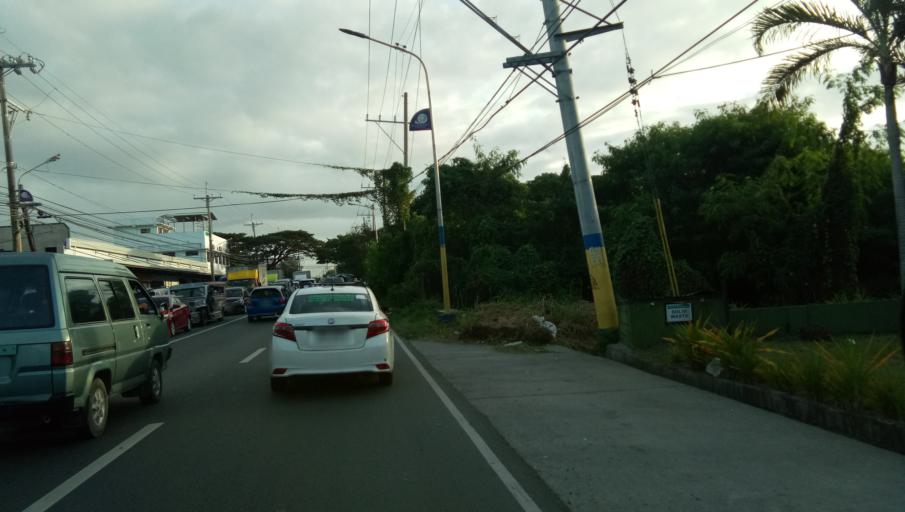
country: PH
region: Calabarzon
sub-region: Province of Cavite
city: Dasmarinas
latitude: 14.3783
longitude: 120.9790
